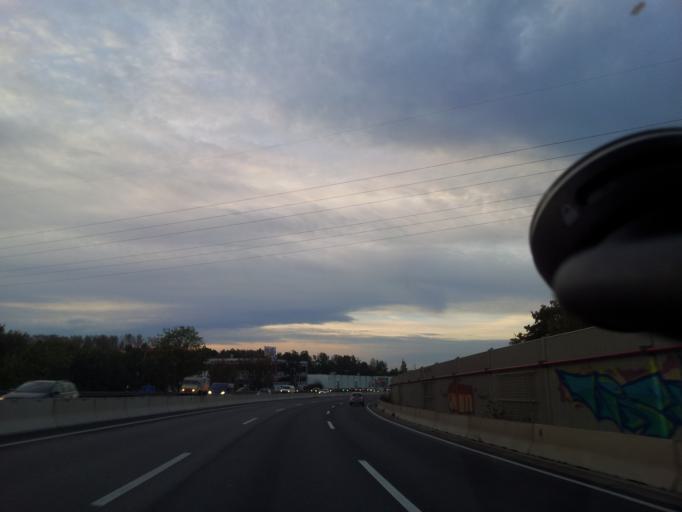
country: DE
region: Lower Saxony
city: Braunschweig
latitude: 52.2444
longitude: 10.5090
